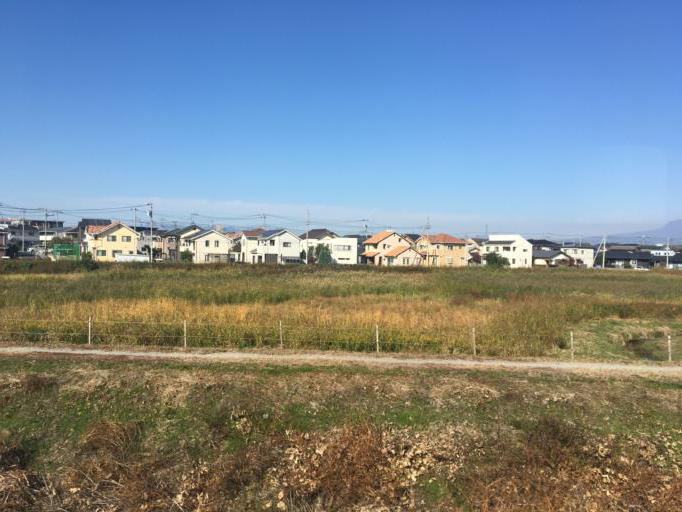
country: JP
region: Gunma
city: Isesaki
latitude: 36.3345
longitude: 139.2148
